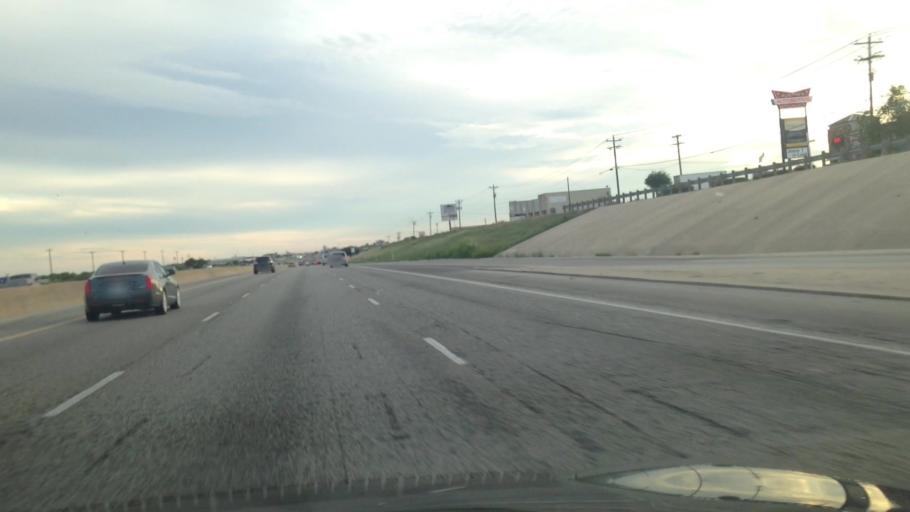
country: US
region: Texas
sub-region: Hays County
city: Buda
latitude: 30.0676
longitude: -97.8298
